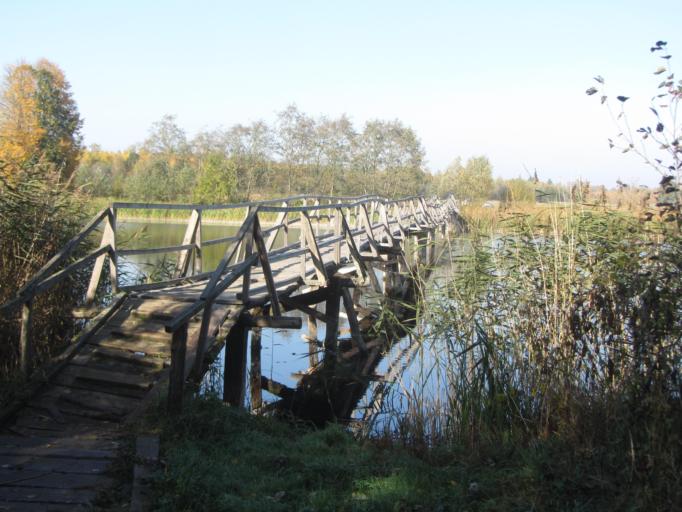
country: LT
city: Ariogala
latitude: 55.3922
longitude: 23.3324
